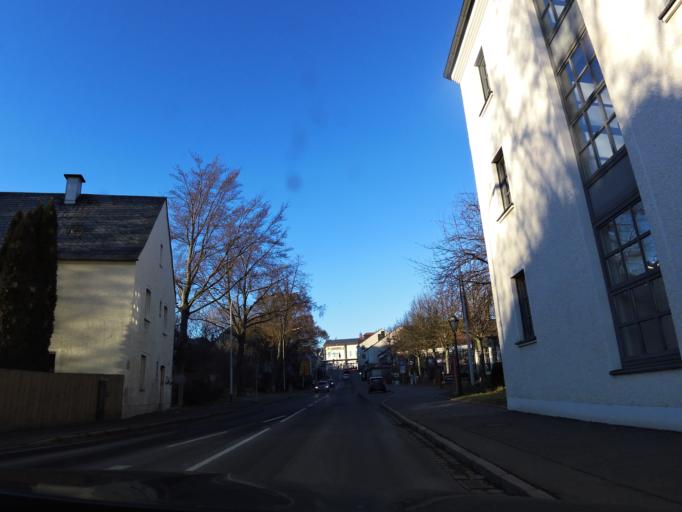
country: DE
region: Bavaria
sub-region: Upper Franconia
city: Wunsiedel
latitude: 50.0373
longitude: 12.0059
